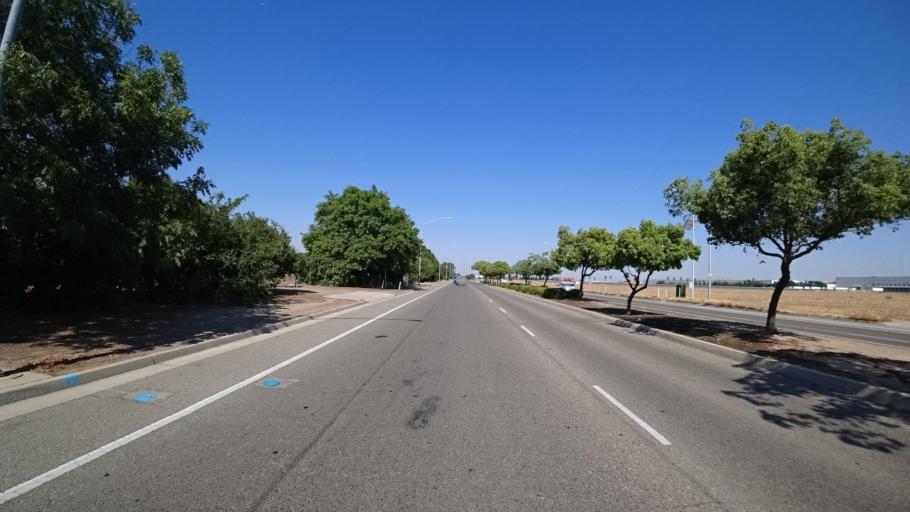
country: US
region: California
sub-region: Fresno County
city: Tarpey Village
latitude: 36.7794
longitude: -119.7030
